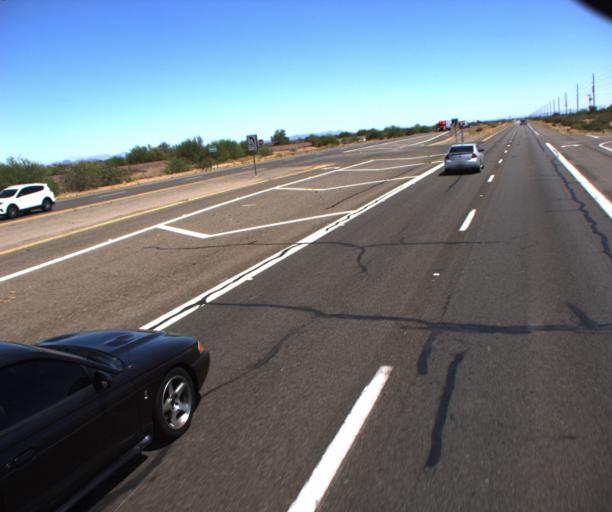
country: US
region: Arizona
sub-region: Maricopa County
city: Sun City West
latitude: 33.7267
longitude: -112.4633
